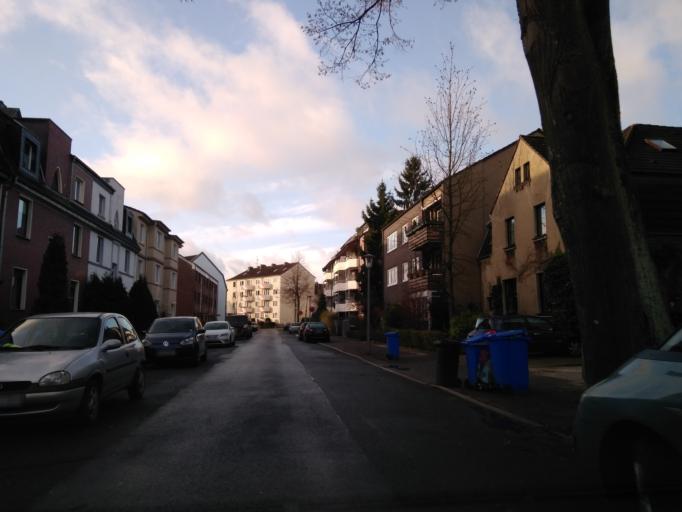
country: DE
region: North Rhine-Westphalia
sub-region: Regierungsbezirk Munster
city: Gladbeck
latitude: 51.5734
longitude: 7.0020
